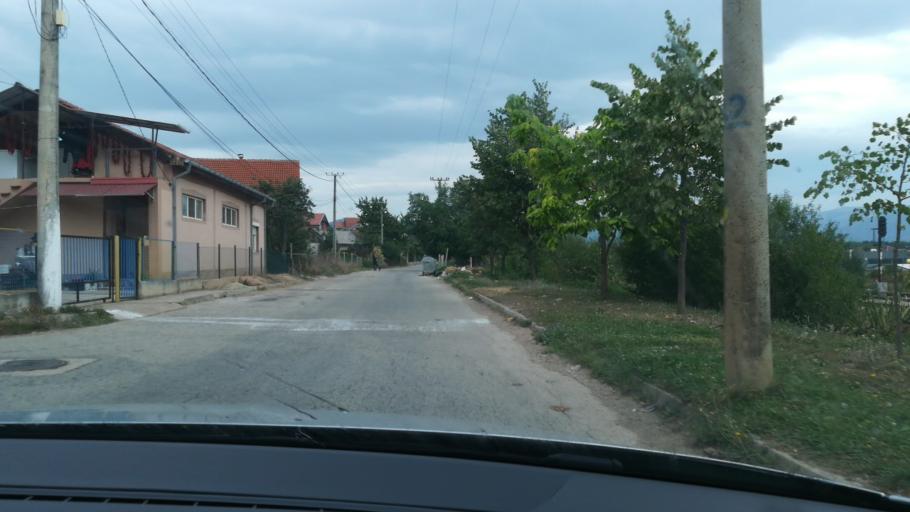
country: MK
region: Kicevo
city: Kicevo
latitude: 41.5142
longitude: 20.9497
